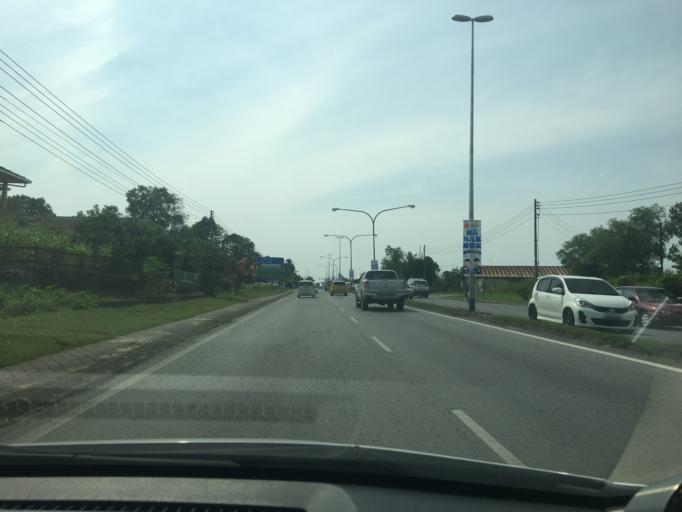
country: MY
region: Sarawak
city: Kuching
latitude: 1.5084
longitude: 110.2884
